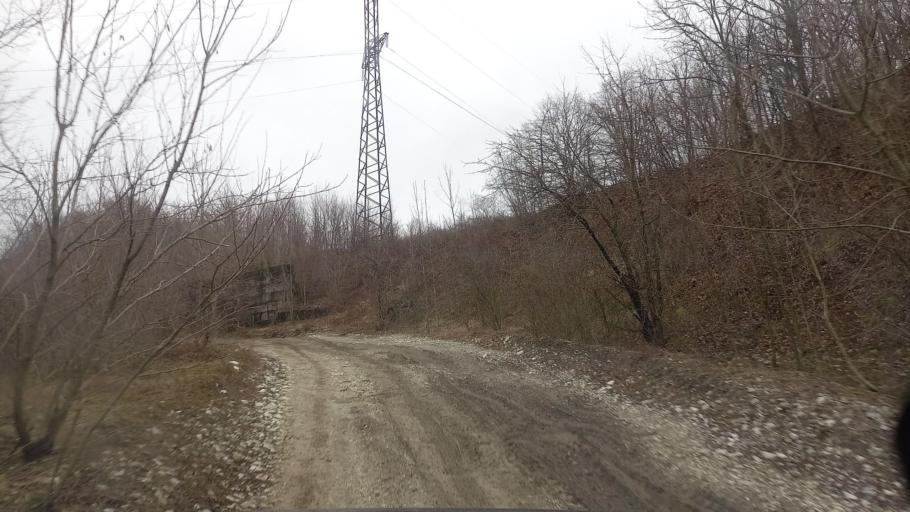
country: RU
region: Krasnodarskiy
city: Divnomorskoye
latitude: 44.5489
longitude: 38.2386
